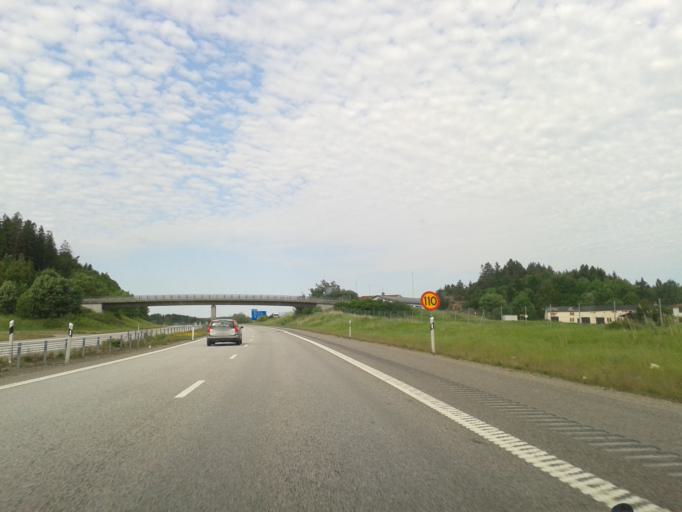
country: SE
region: Vaestra Goetaland
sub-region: Munkedals Kommun
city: Munkedal
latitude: 58.4902
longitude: 11.6125
